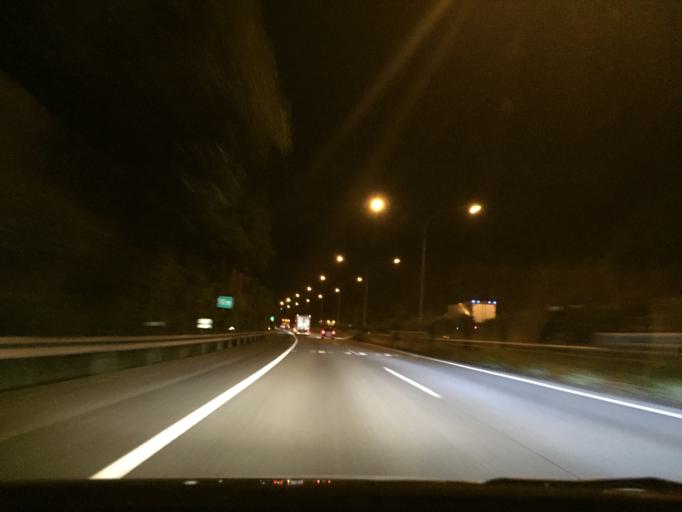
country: JP
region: Kanagawa
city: Hadano
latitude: 35.3531
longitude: 139.1239
